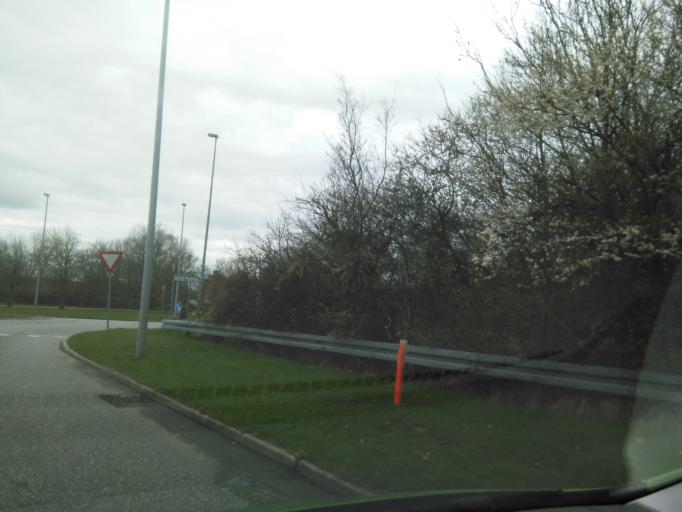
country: DK
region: Central Jutland
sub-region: Arhus Kommune
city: Stavtrup
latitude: 56.1756
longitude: 10.1196
